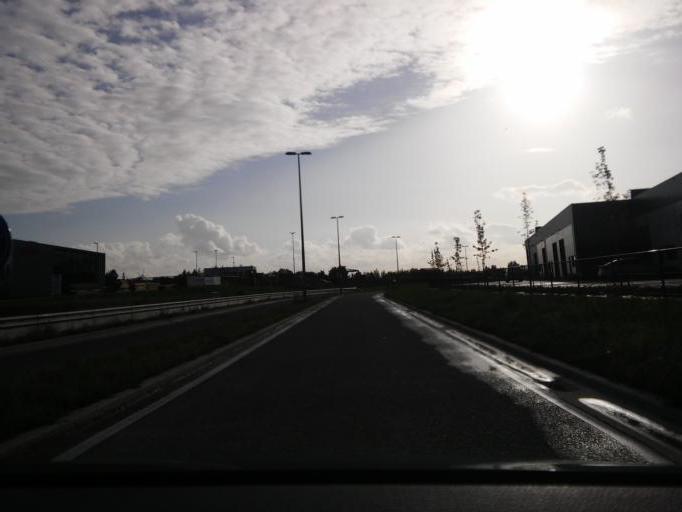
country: BE
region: Flanders
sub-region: Provincie Antwerpen
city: Boom
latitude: 51.1047
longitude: 4.3608
